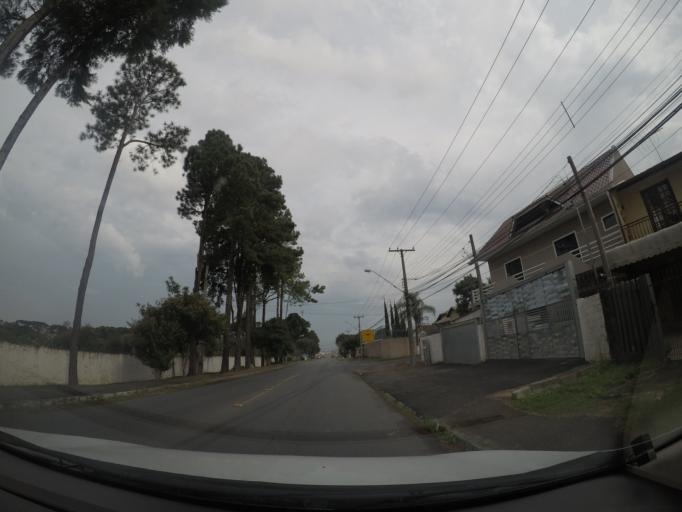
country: BR
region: Parana
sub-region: Sao Jose Dos Pinhais
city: Sao Jose dos Pinhais
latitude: -25.5168
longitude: -49.2612
